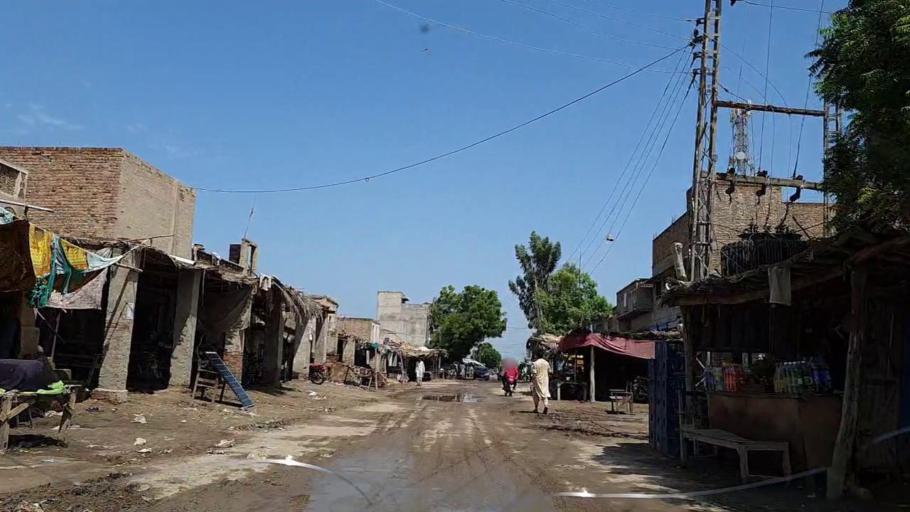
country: PK
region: Sindh
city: Naushahro Firoz
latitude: 26.8109
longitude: 68.1962
